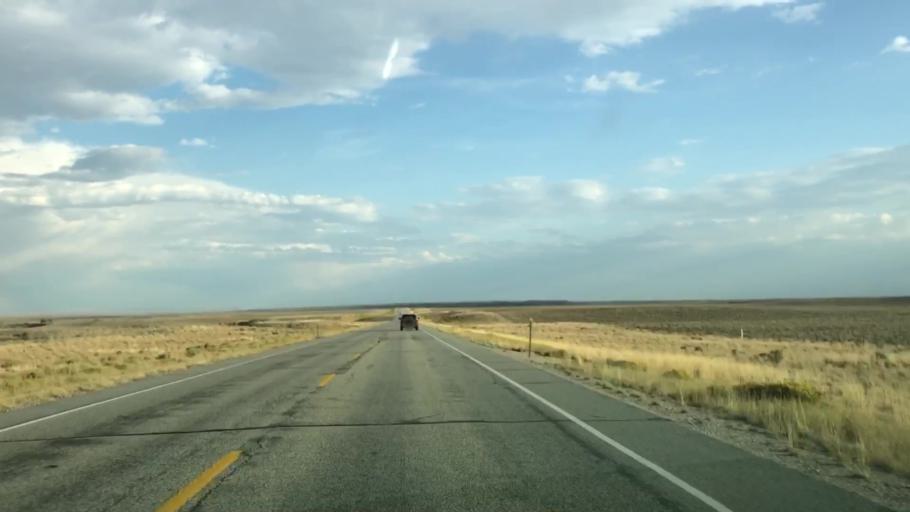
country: US
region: Wyoming
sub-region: Sublette County
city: Marbleton
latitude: 42.3316
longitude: -109.5166
